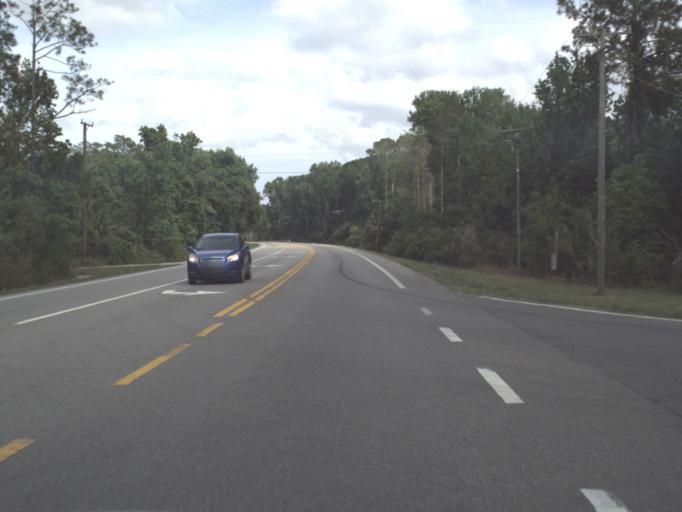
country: US
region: Florida
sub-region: Flagler County
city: Bunnell
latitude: 29.4687
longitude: -81.3147
